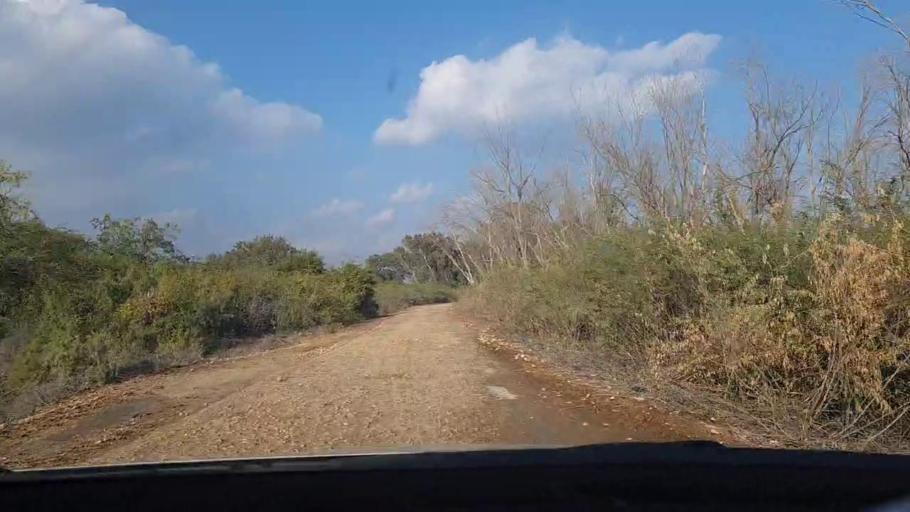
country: PK
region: Sindh
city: Tando Mittha Khan
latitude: 25.8995
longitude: 69.3025
